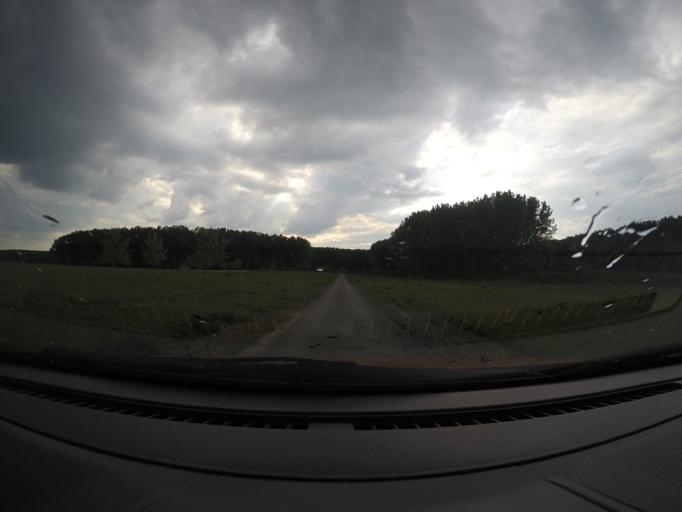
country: RS
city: Orlovat
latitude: 45.2064
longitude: 20.5837
